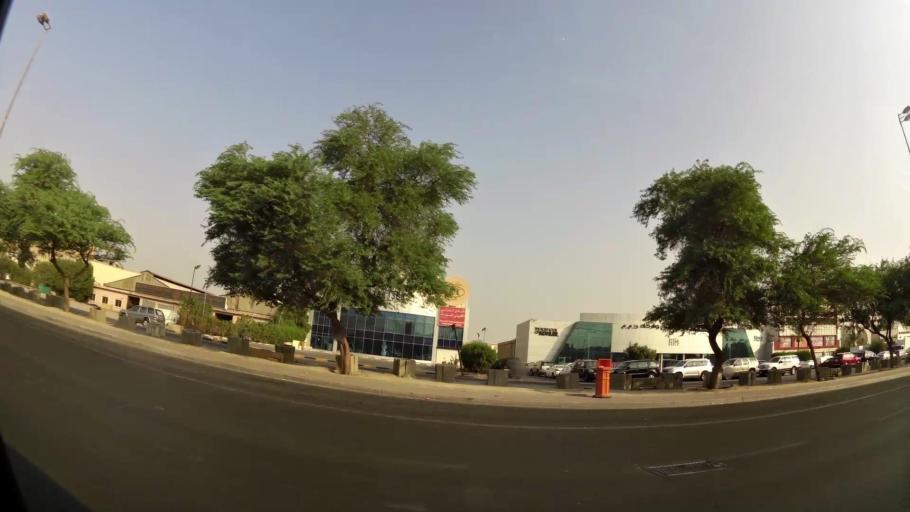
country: KW
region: Al Asimah
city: Ar Rabiyah
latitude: 29.3143
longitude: 47.9360
